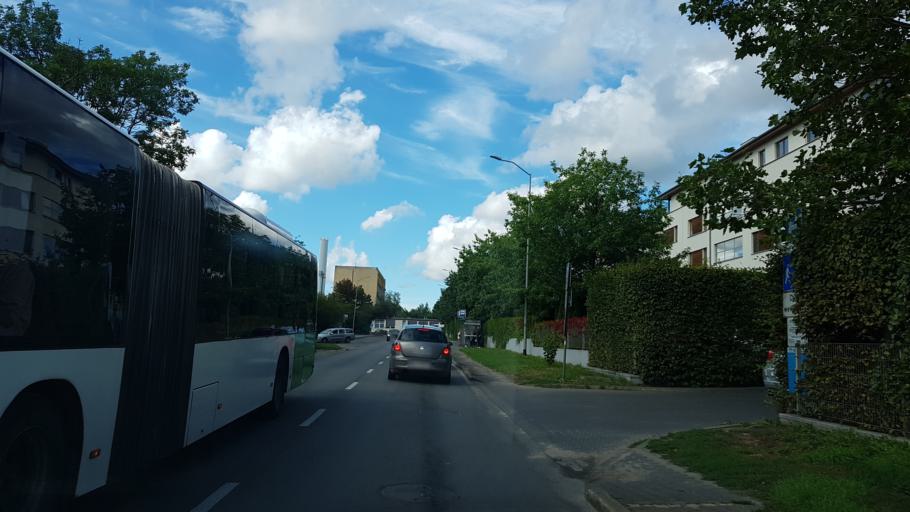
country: PL
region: West Pomeranian Voivodeship
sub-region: Szczecin
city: Szczecin
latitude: 53.4486
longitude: 14.4969
